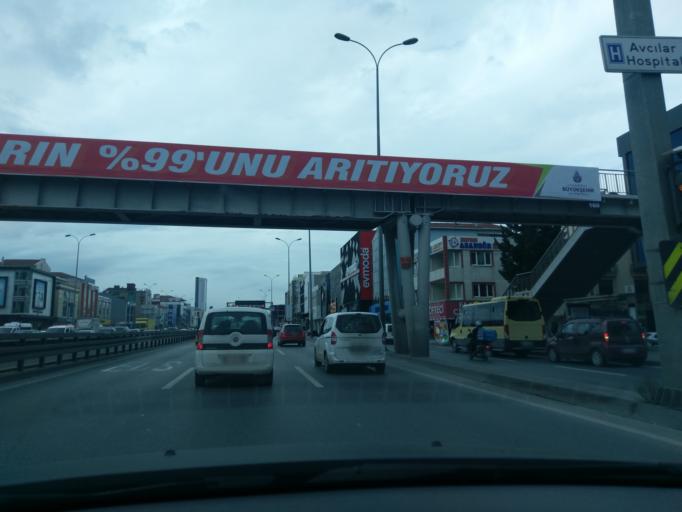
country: TR
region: Istanbul
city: Yakuplu
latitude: 40.9885
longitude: 28.7176
